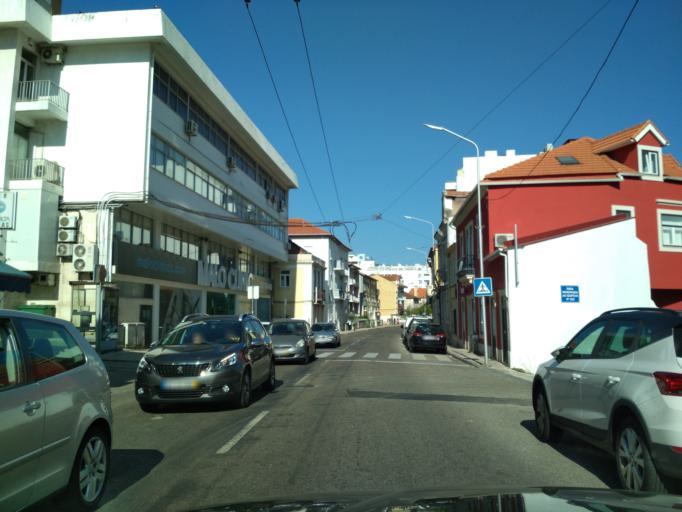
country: PT
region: Coimbra
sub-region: Coimbra
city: Coimbra
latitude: 40.2019
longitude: -8.4137
